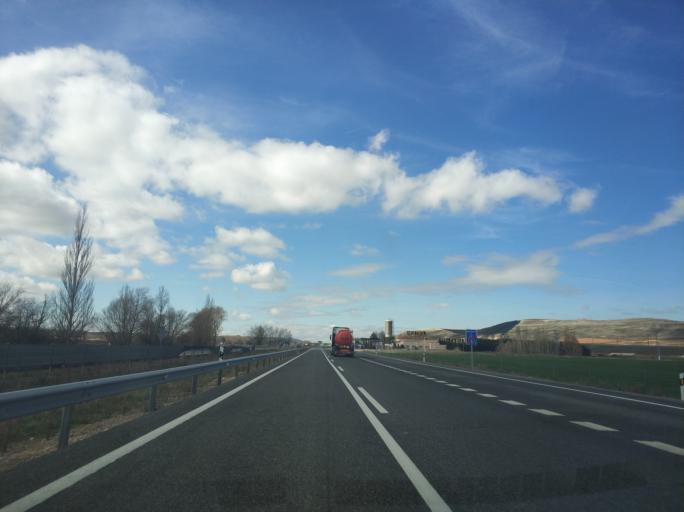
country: ES
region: Castille and Leon
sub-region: Provincia de Burgos
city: Frandovinez
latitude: 42.2957
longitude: -3.8426
